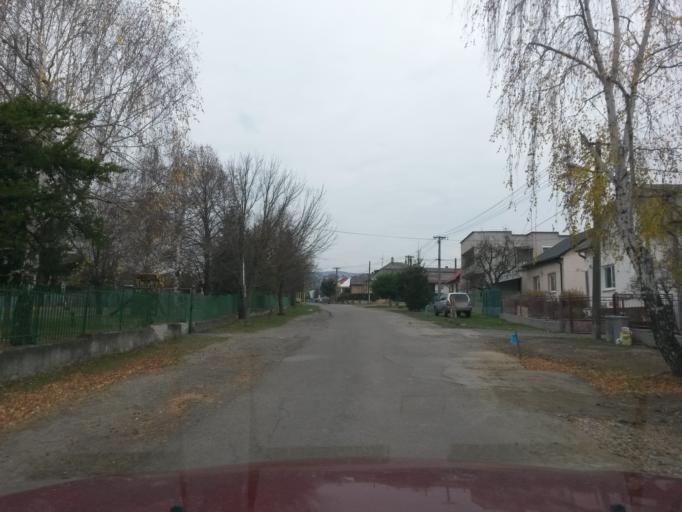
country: SK
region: Kosicky
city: Secovce
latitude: 48.7057
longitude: 21.6526
